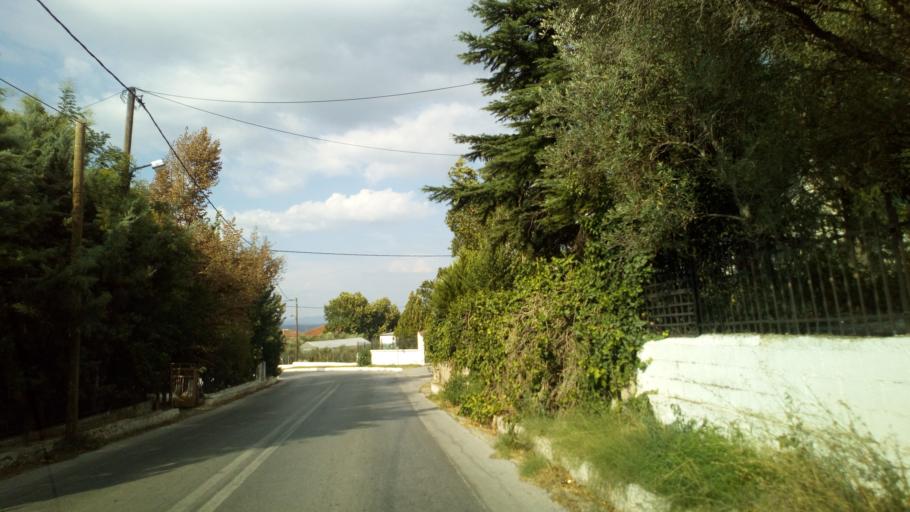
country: GR
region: Central Macedonia
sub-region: Nomos Thessalonikis
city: Gerakarou
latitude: 40.6272
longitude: 23.2182
